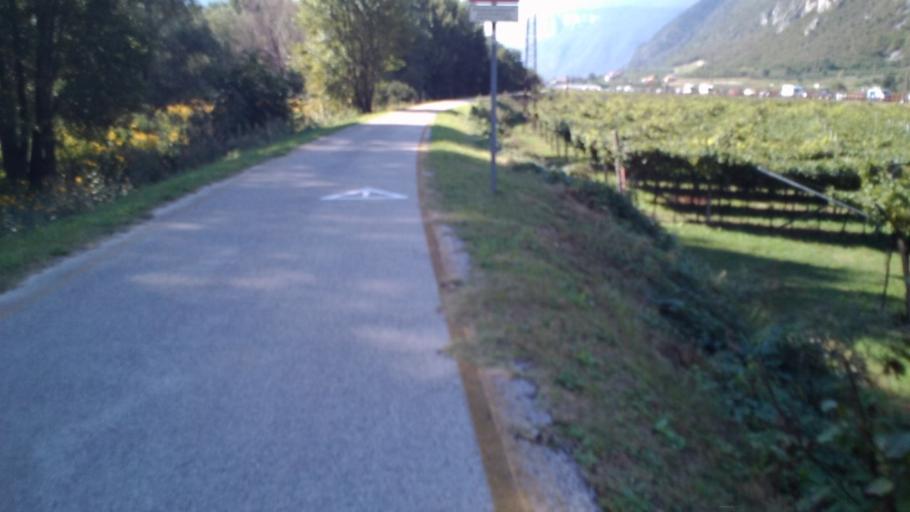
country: IT
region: Trentino-Alto Adige
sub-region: Provincia di Trento
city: Avio
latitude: 45.7164
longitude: 10.9339
